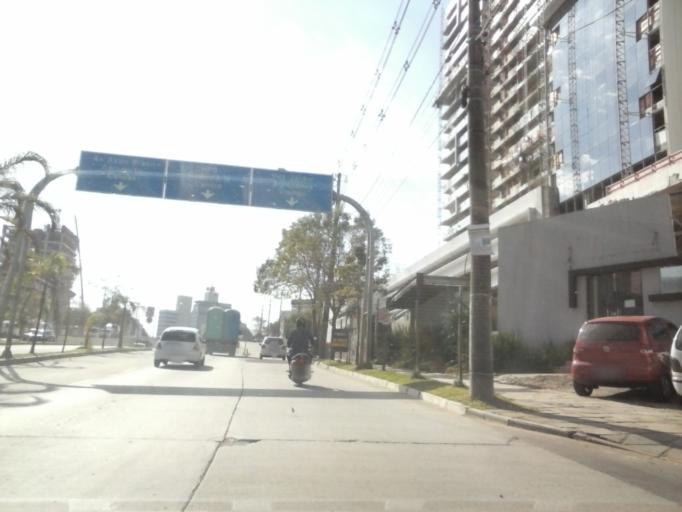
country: BR
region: Rio Grande do Sul
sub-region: Porto Alegre
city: Porto Alegre
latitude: -30.0415
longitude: -51.1731
